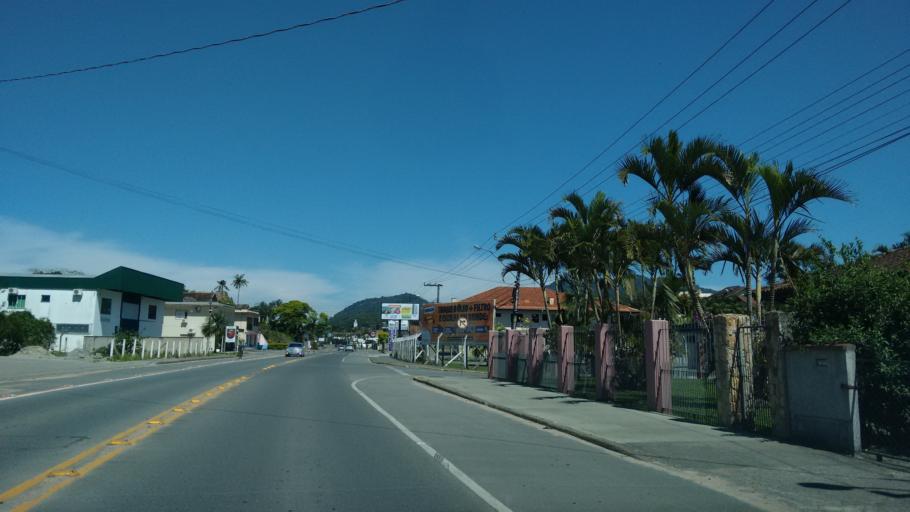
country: BR
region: Santa Catarina
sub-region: Pomerode
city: Pomerode
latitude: -26.7470
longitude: -49.1739
